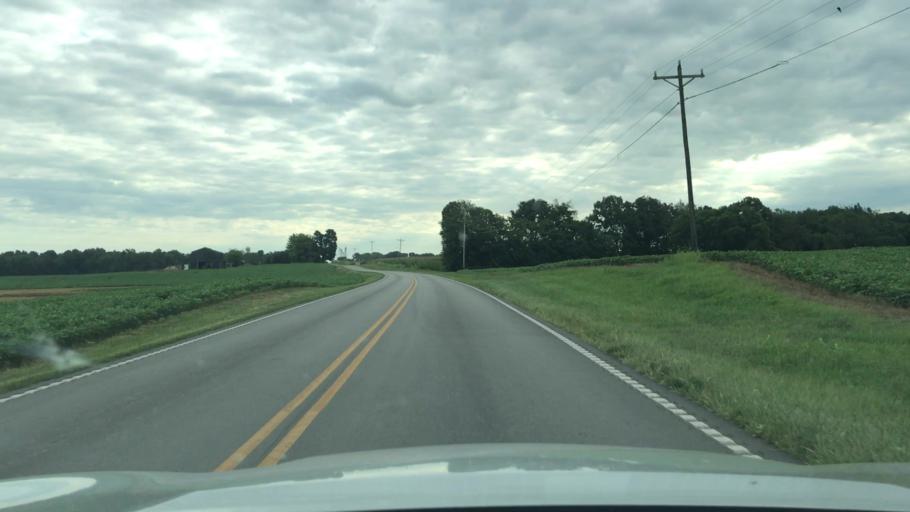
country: US
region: Kentucky
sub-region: Todd County
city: Elkton
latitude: 36.7417
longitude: -87.1804
